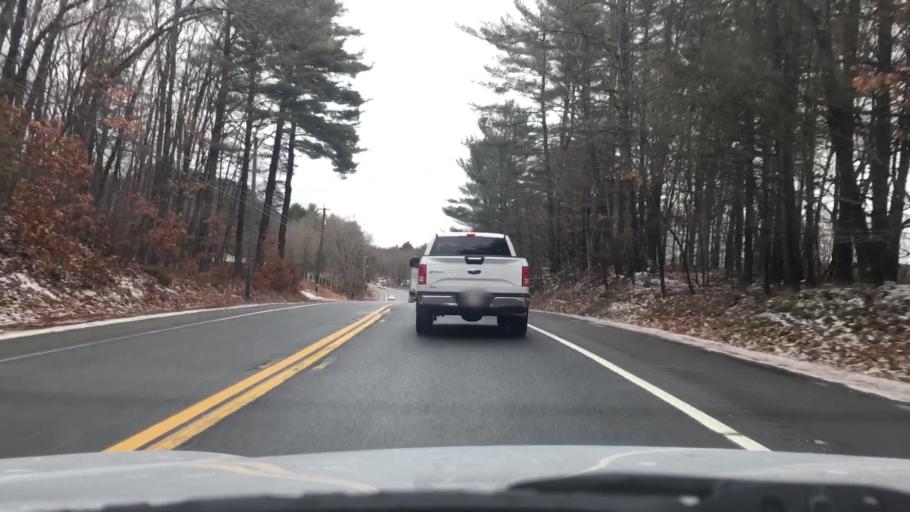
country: US
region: Massachusetts
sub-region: Franklin County
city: Turners Falls
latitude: 42.6060
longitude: -72.5271
